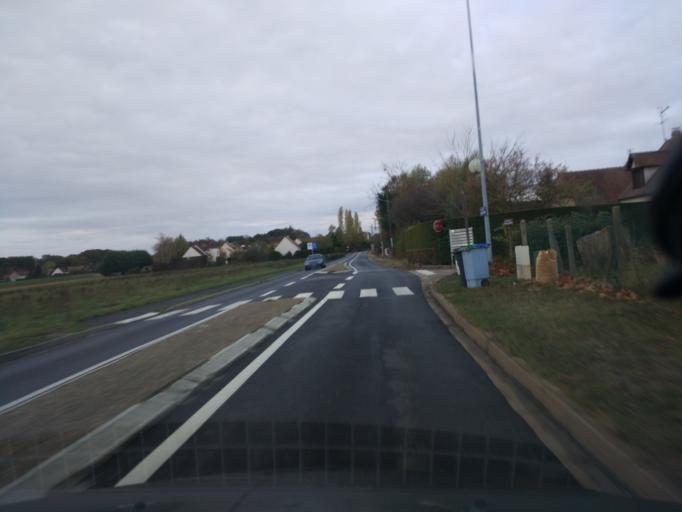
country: FR
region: Ile-de-France
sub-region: Departement de l'Essonne
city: Les Molieres
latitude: 48.6783
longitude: 2.0732
